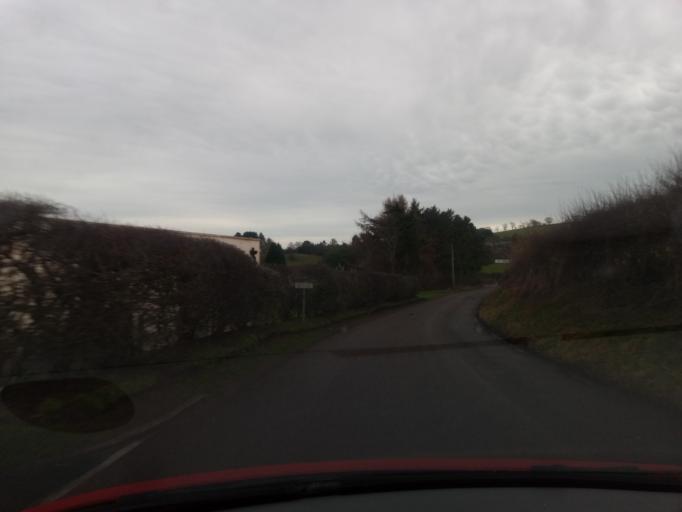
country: GB
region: England
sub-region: Northumberland
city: Wooler
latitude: 55.5509
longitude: -2.0287
